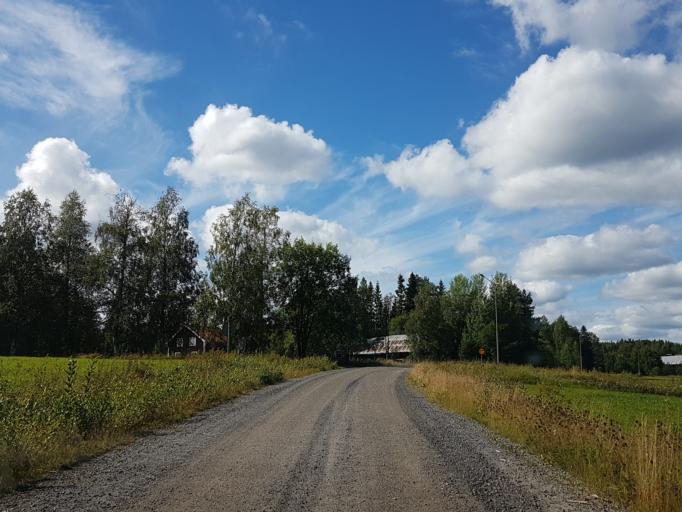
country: SE
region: Vaesterbotten
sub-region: Skelleftea Kommun
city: Burtraesk
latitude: 64.2908
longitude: 20.4547
